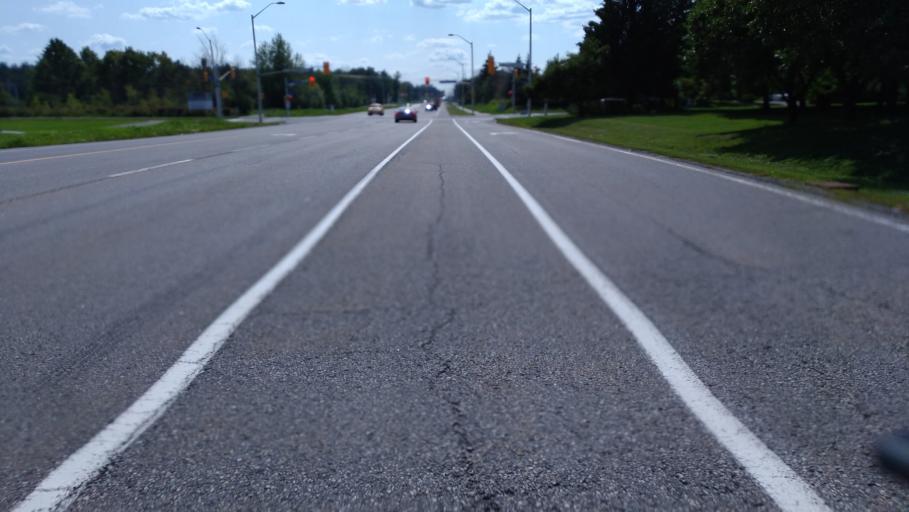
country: CA
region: Ontario
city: Bells Corners
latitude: 45.3456
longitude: -75.9303
